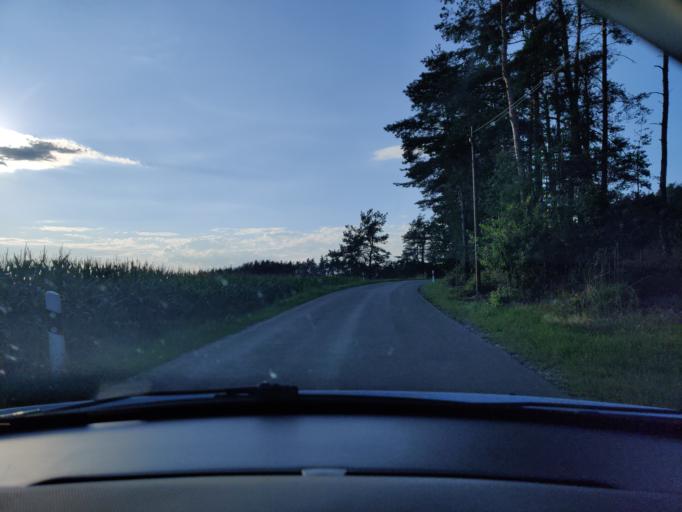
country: DE
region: Bavaria
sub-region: Upper Palatinate
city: Nabburg
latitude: 49.4175
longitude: 12.1743
